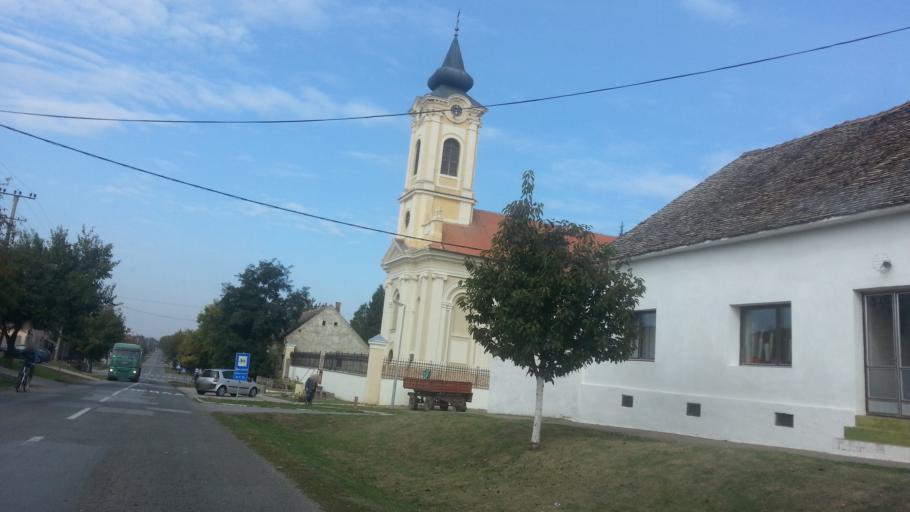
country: RS
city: Surduk
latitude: 45.0703
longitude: 20.3264
